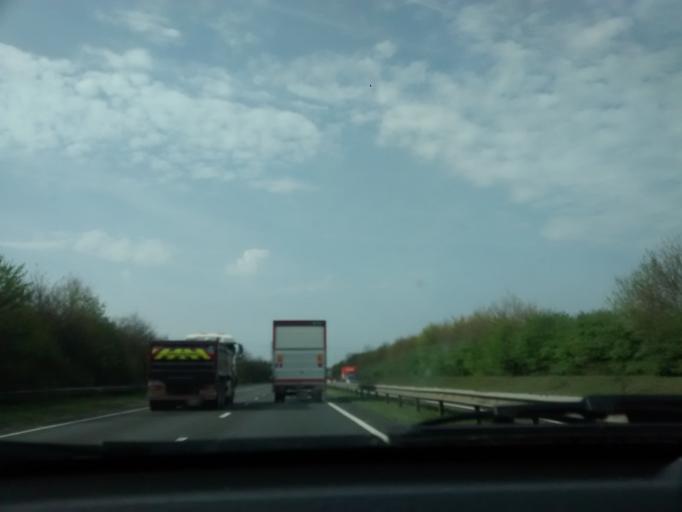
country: GB
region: England
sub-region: Oxfordshire
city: Kidlington
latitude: 51.8070
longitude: -1.2723
